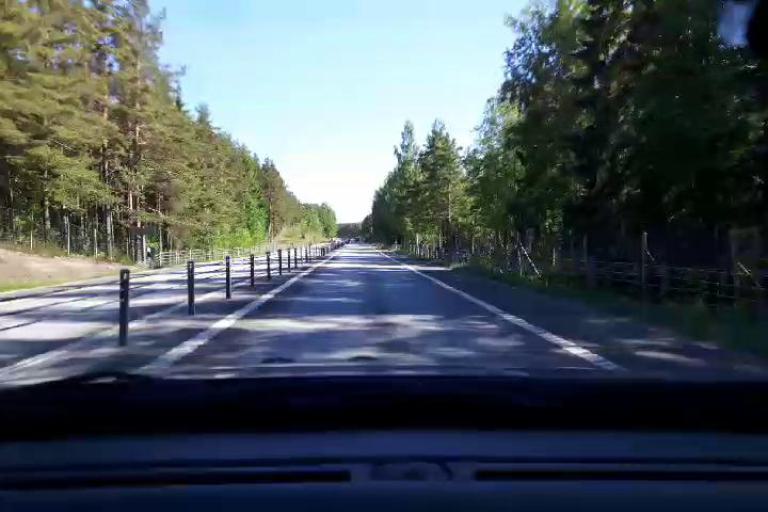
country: SE
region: Gaevleborg
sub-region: Gavle Kommun
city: Norrsundet
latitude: 61.0022
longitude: 16.9896
